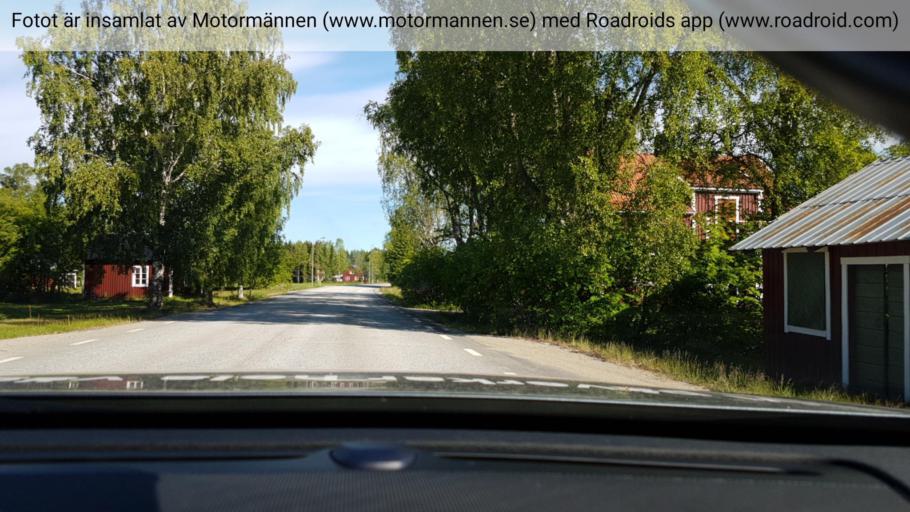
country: SE
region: Vaesterbotten
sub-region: Vindelns Kommun
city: Vindeln
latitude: 64.1192
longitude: 19.5639
